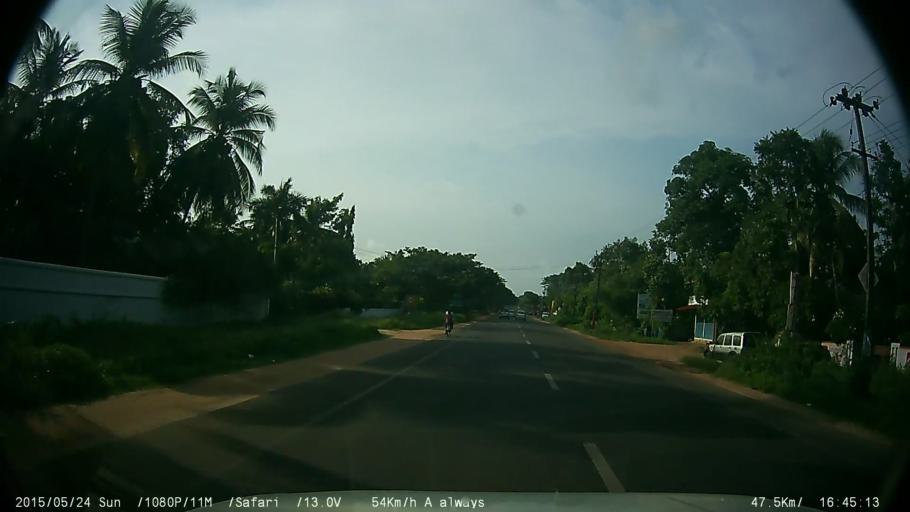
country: IN
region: Kerala
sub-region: Alappuzha
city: Shertallai
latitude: 9.6594
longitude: 76.3379
